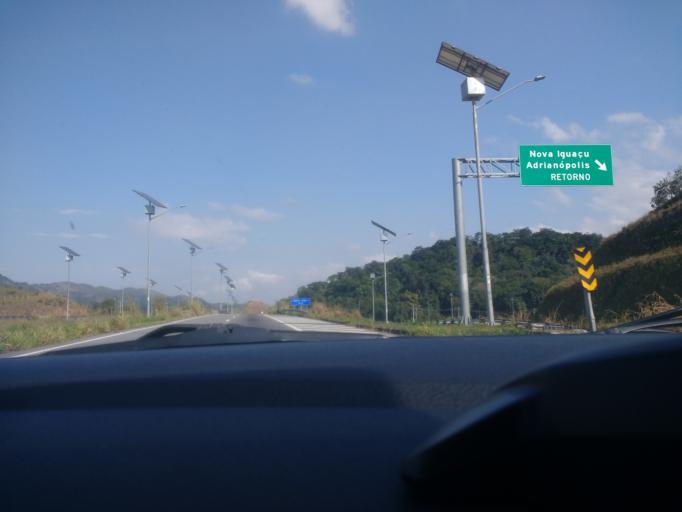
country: BR
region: Rio de Janeiro
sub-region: Nova Iguacu
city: Nova Iguacu
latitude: -22.6831
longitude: -43.4770
